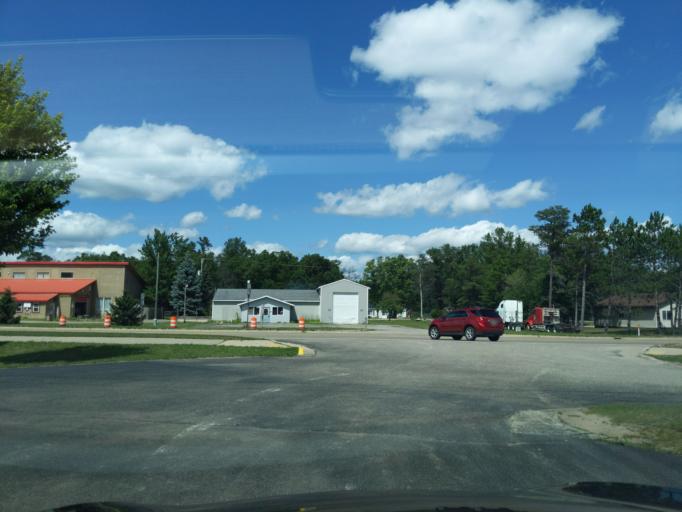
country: US
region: Michigan
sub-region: Crawford County
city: Grayling
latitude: 44.6552
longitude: -84.7360
